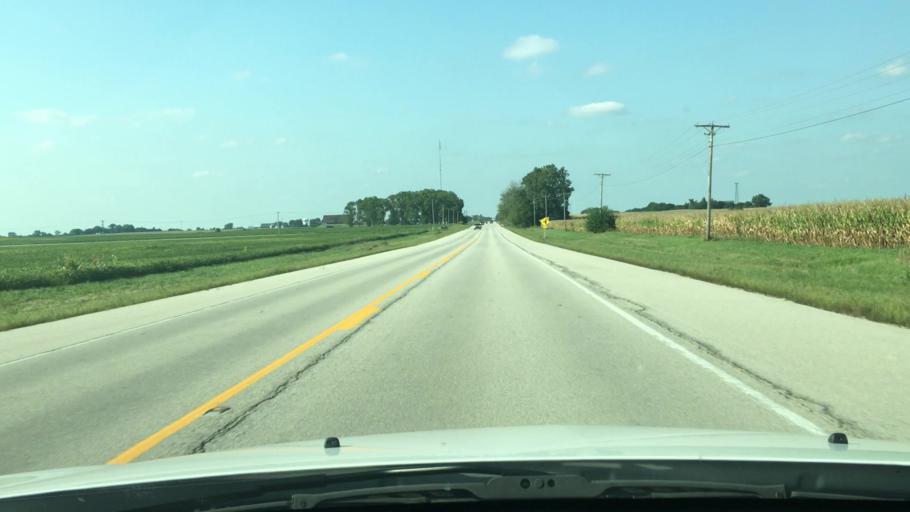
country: US
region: Illinois
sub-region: DeKalb County
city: DeKalb
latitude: 41.8608
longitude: -88.7538
